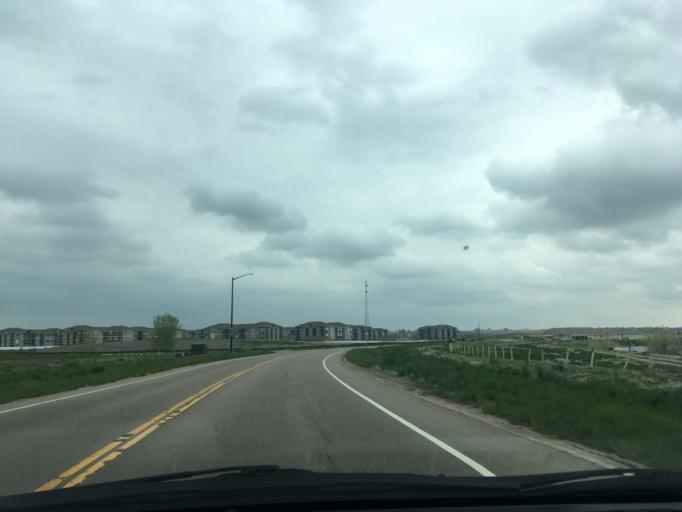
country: US
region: Colorado
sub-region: Weld County
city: Firestone
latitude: 40.1625
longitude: -104.9710
